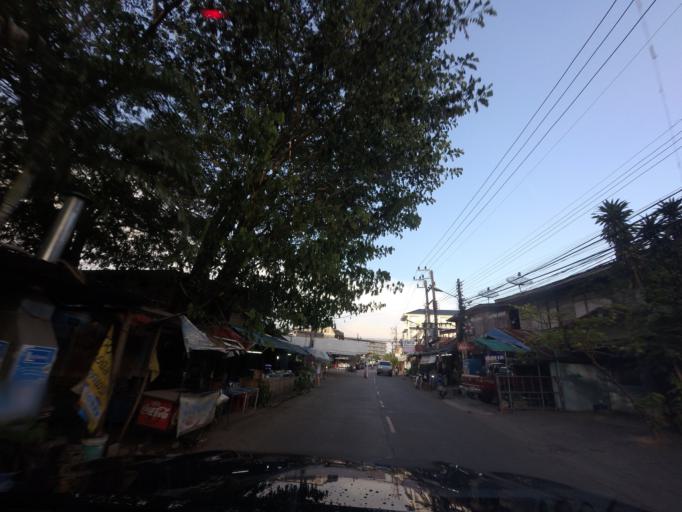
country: TH
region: Khon Kaen
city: Khon Kaen
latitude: 16.4308
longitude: 102.8560
